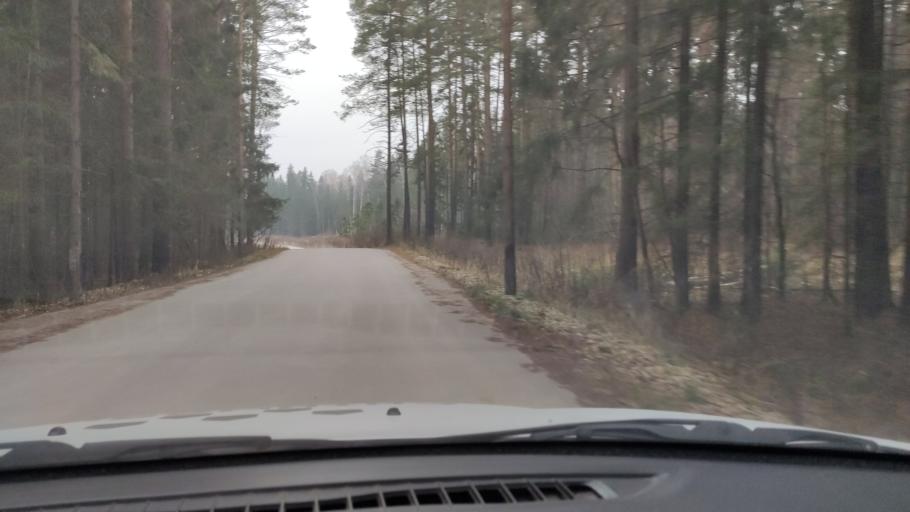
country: RU
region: Perm
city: Kondratovo
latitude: 58.0473
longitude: 56.1456
